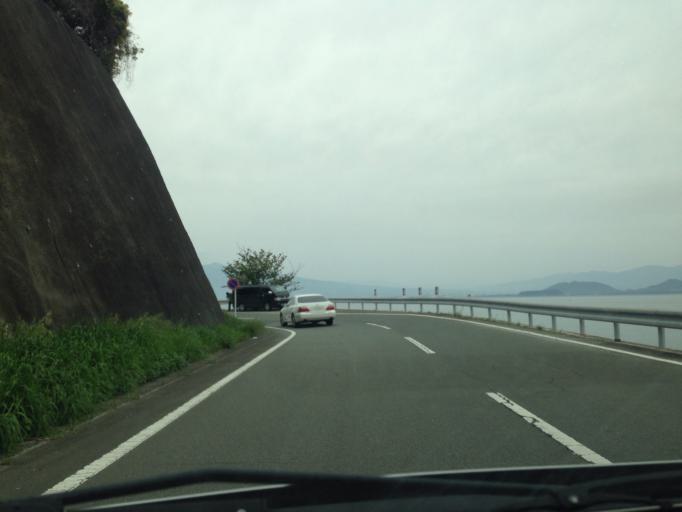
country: JP
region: Shizuoka
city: Heda
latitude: 35.0192
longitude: 138.8341
